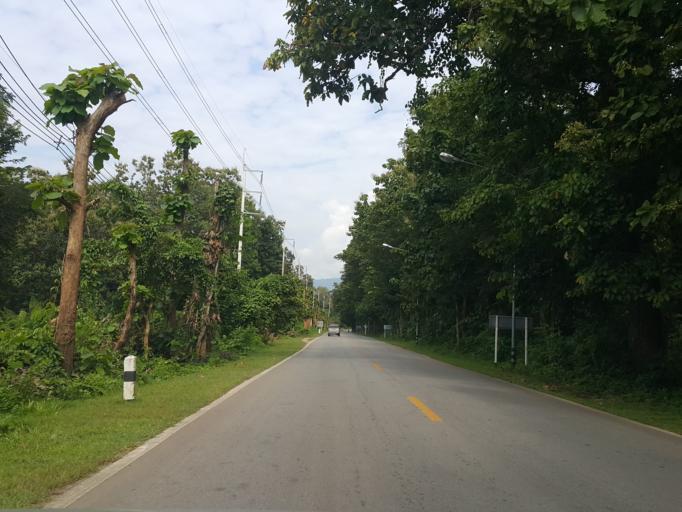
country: TH
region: Mae Hong Son
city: Mae Hong Son
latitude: 19.3685
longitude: 97.9643
